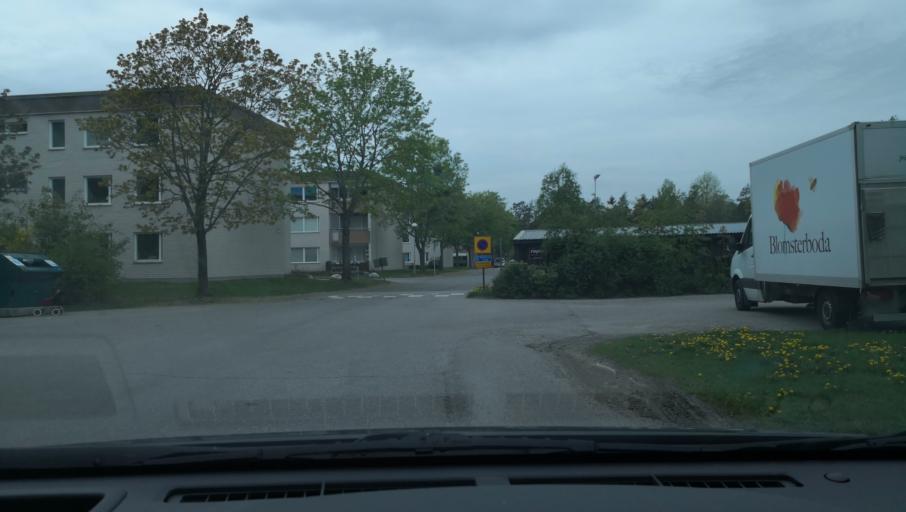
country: SE
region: Stockholm
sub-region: Upplands-Bro Kommun
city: Kungsaengen
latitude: 59.4905
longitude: 17.7365
